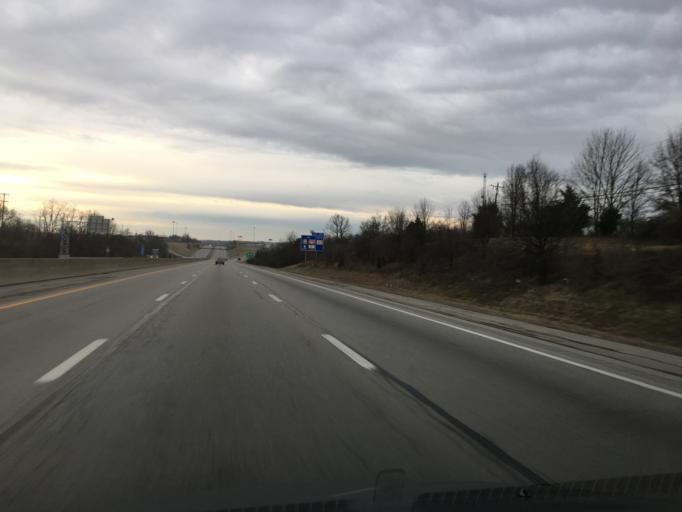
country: US
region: Kentucky
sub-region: Boone County
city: Walton
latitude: 38.8674
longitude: -84.6241
